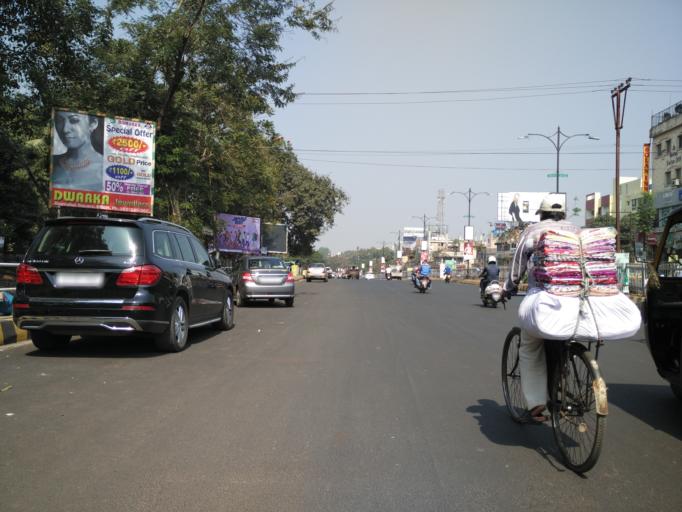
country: IN
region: Odisha
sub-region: Khordha
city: Bhubaneshwar
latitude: 20.2707
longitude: 85.8418
